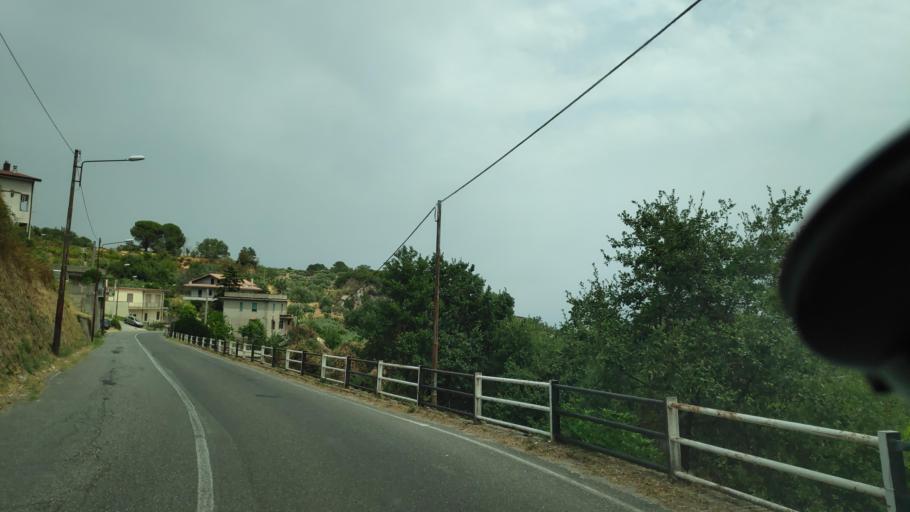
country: IT
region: Calabria
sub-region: Provincia di Catanzaro
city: Davoli
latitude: 38.6521
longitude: 16.4863
